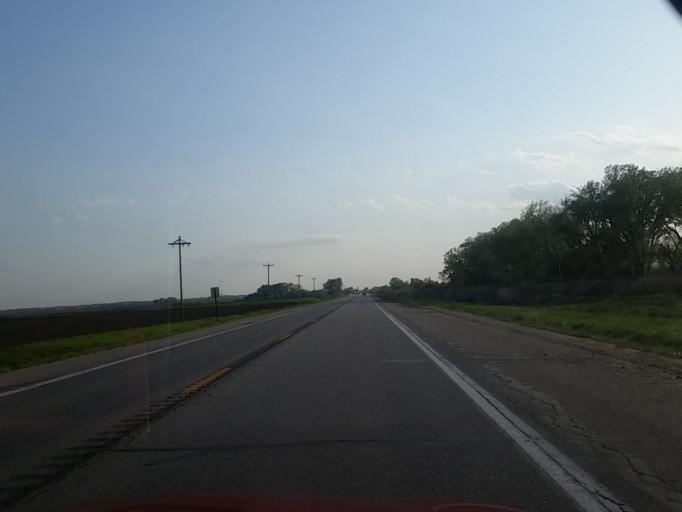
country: US
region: Nebraska
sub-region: Sarpy County
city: Gretna
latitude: 41.0818
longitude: -96.2917
